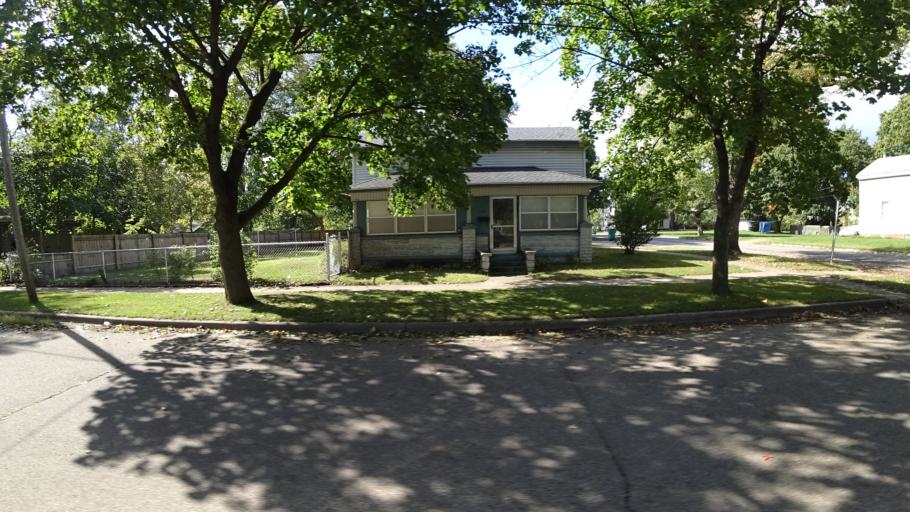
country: US
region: Michigan
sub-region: Saint Joseph County
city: Three Rivers
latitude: 41.9319
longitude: -85.6297
